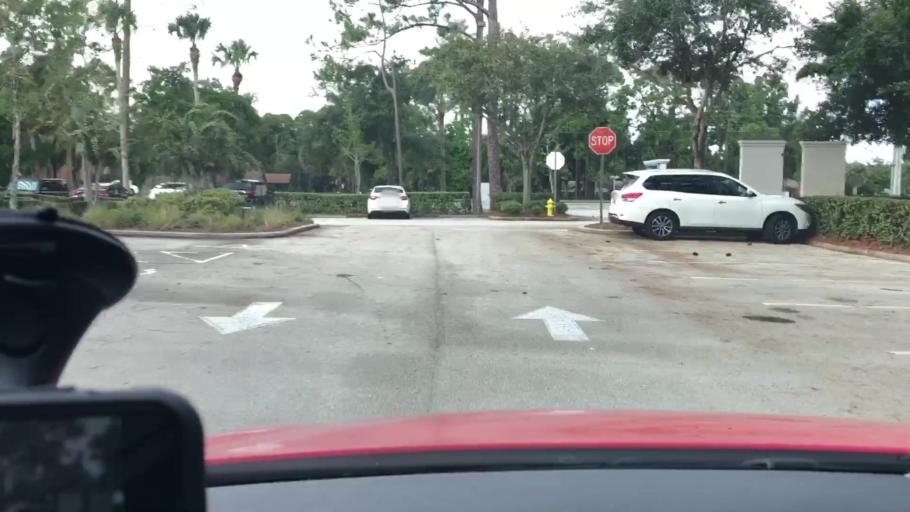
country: US
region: Florida
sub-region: Volusia County
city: Port Orange
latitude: 29.1327
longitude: -80.9999
